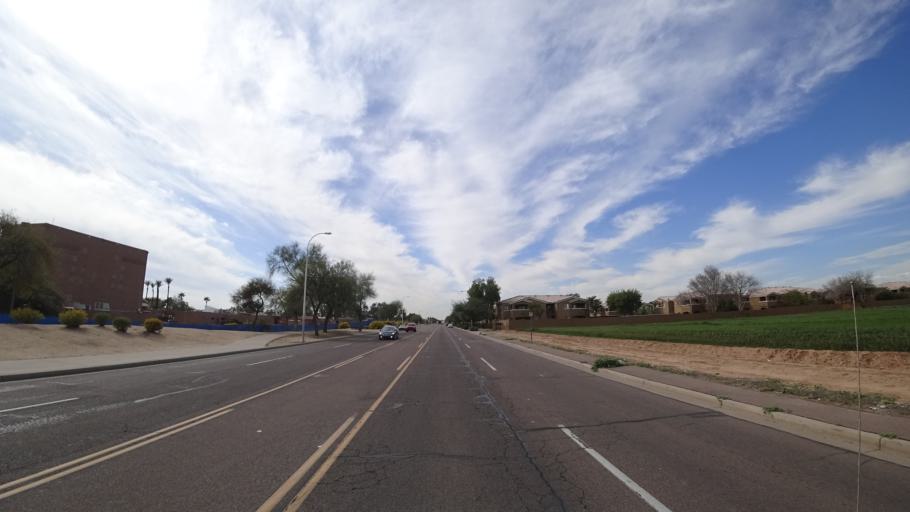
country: US
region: Arizona
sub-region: Maricopa County
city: Tolleson
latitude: 33.4727
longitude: -112.2319
